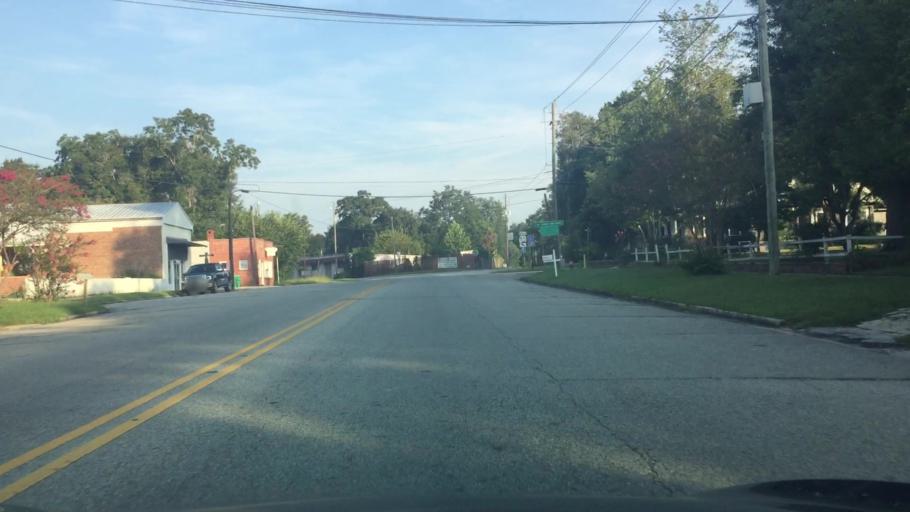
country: US
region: Alabama
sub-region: Covington County
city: Florala
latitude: 31.0084
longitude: -86.3332
